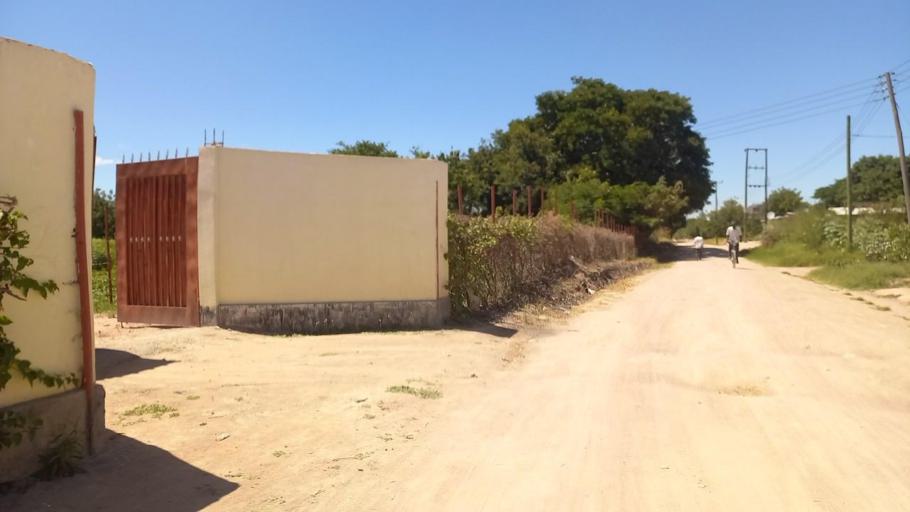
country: TZ
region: Dodoma
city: Dodoma
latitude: -6.1301
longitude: 35.7375
